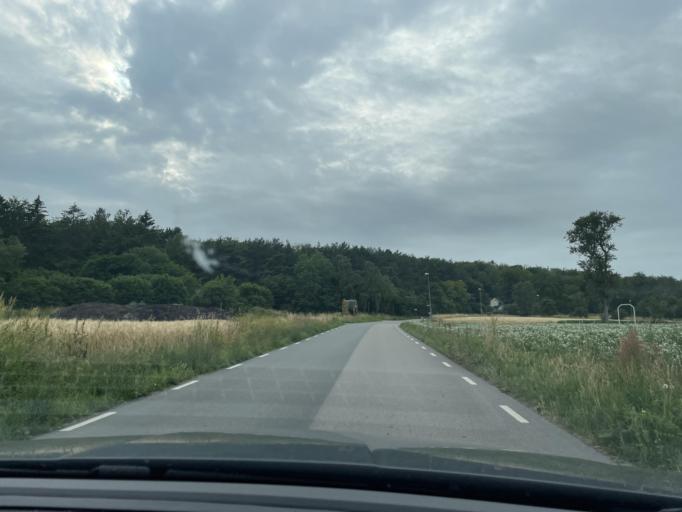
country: SE
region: Blekinge
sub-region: Solvesborgs Kommun
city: Soelvesborg
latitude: 56.0258
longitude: 14.6384
